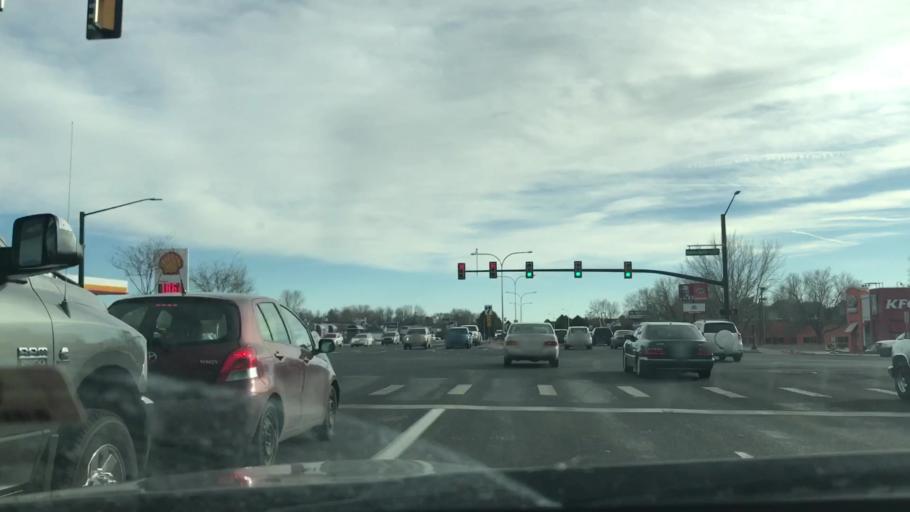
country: US
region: Colorado
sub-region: El Paso County
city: Cimarron Hills
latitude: 38.8911
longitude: -104.7570
